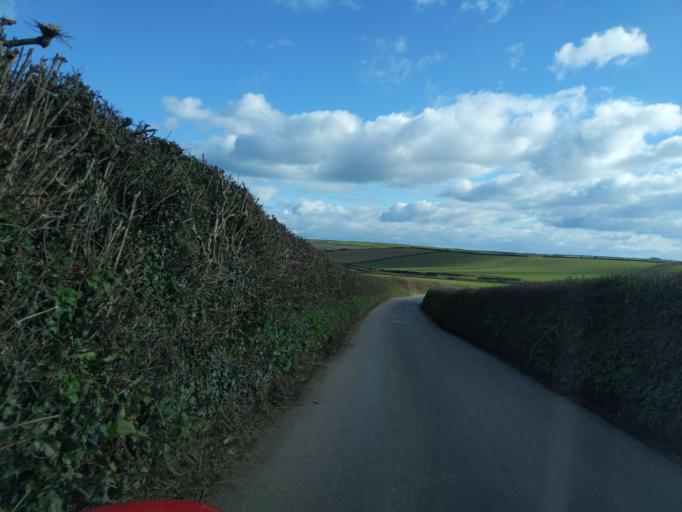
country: GB
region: England
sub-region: Devon
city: Salcombe
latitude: 50.2614
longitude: -3.7166
